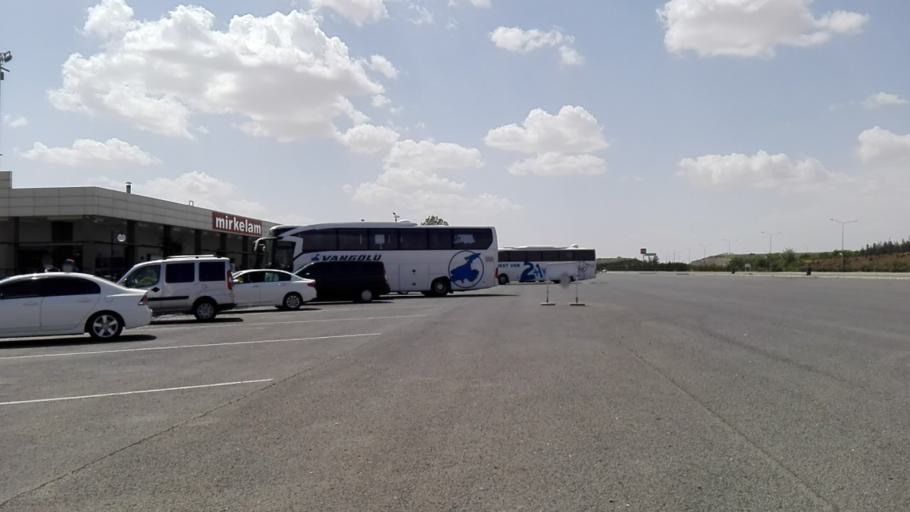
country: TR
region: Sanliurfa
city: Bogurtlen
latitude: 37.0986
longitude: 38.1894
